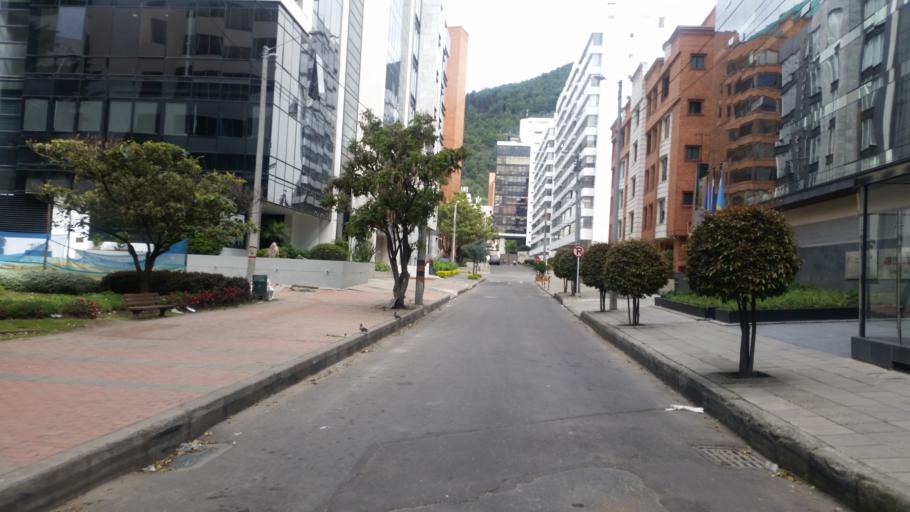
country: CO
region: Bogota D.C.
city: Barrio San Luis
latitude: 4.6808
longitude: -74.0432
